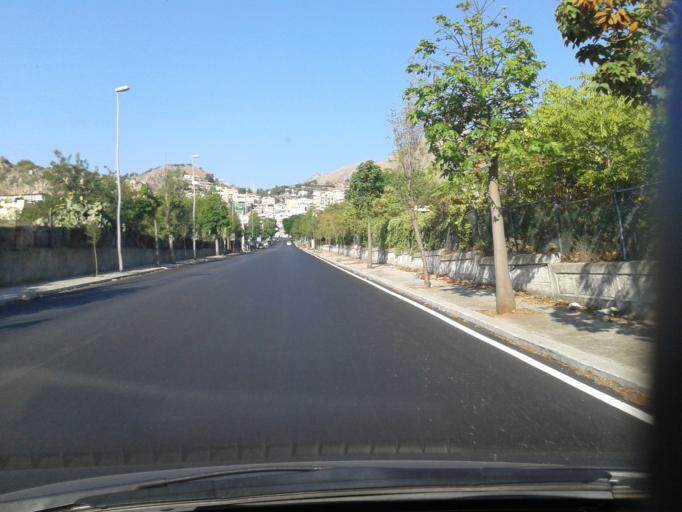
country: IT
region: Sicily
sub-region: Palermo
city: Palermo
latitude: 38.1096
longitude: 13.3135
